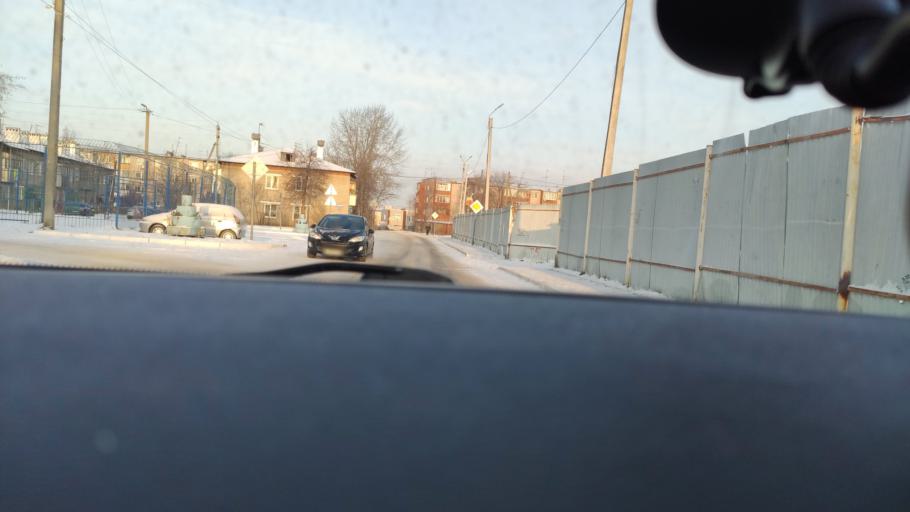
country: RU
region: Perm
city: Kondratovo
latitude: 57.9441
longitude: 56.0665
